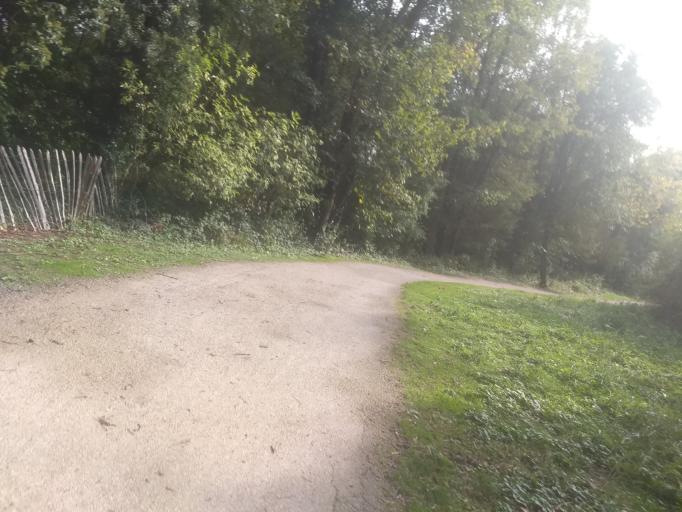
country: FR
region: Nord-Pas-de-Calais
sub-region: Departement du Pas-de-Calais
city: Achicourt
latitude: 50.2817
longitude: 2.7562
